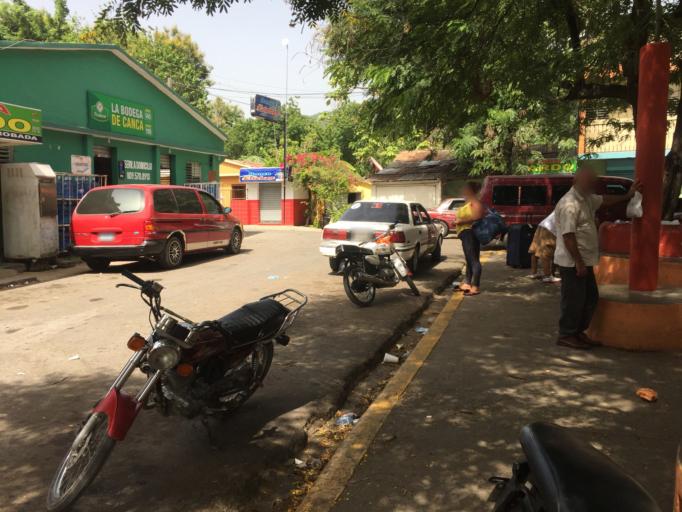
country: DO
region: Santiago
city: Tamboril
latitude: 19.4757
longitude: -70.5839
